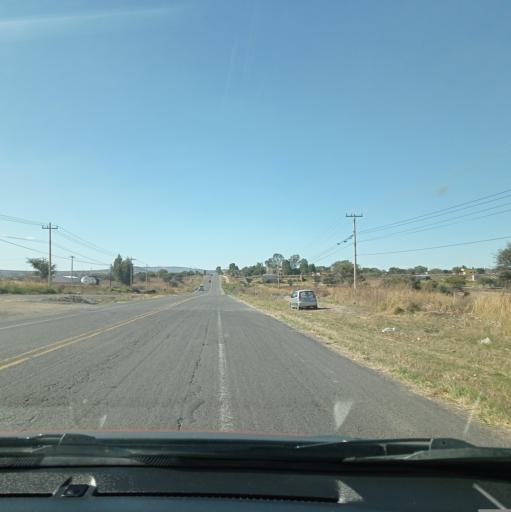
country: MX
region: Jalisco
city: San Miguel el Alto
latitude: 21.0232
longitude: -102.3614
